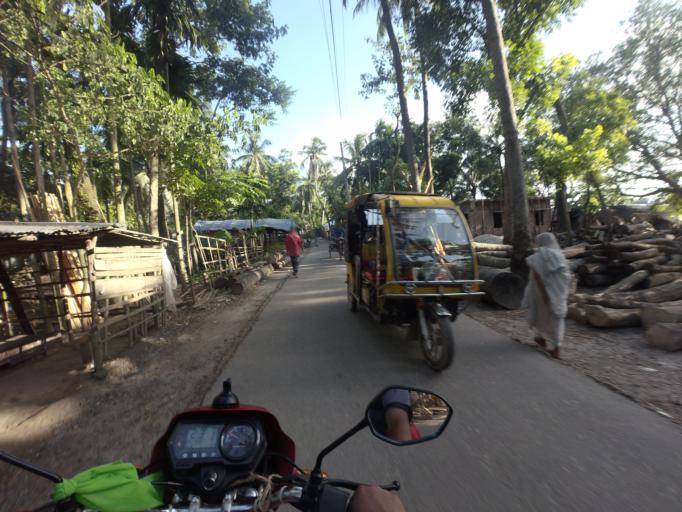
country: BD
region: Khulna
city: Khulna
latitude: 22.9169
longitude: 89.5188
